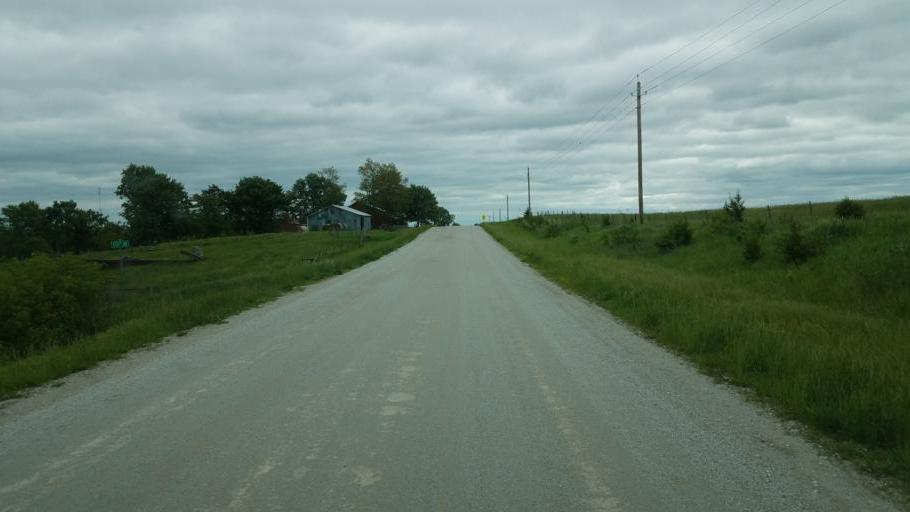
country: US
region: Iowa
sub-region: Decatur County
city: Lamoni
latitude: 40.6381
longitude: -93.8817
